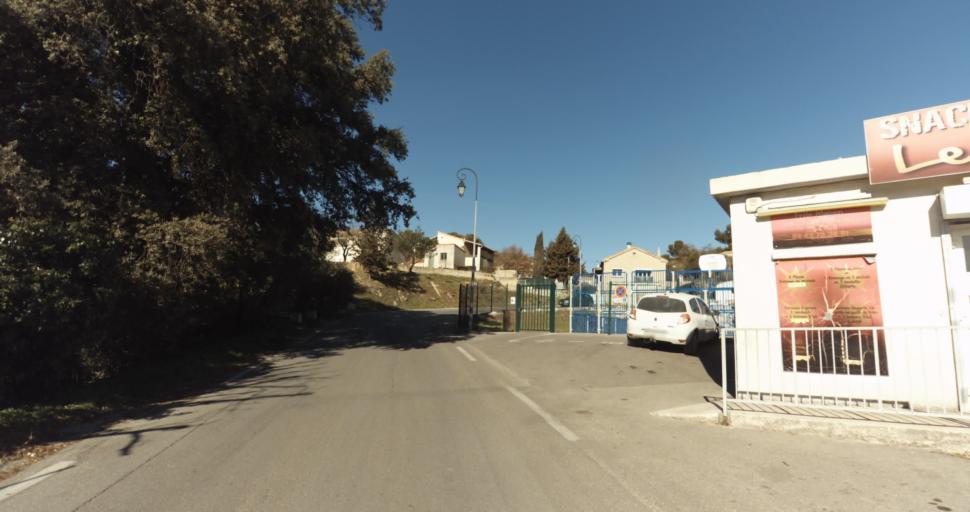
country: FR
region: Provence-Alpes-Cote d'Azur
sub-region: Departement des Bouches-du-Rhone
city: Peypin
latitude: 43.3855
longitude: 5.5781
